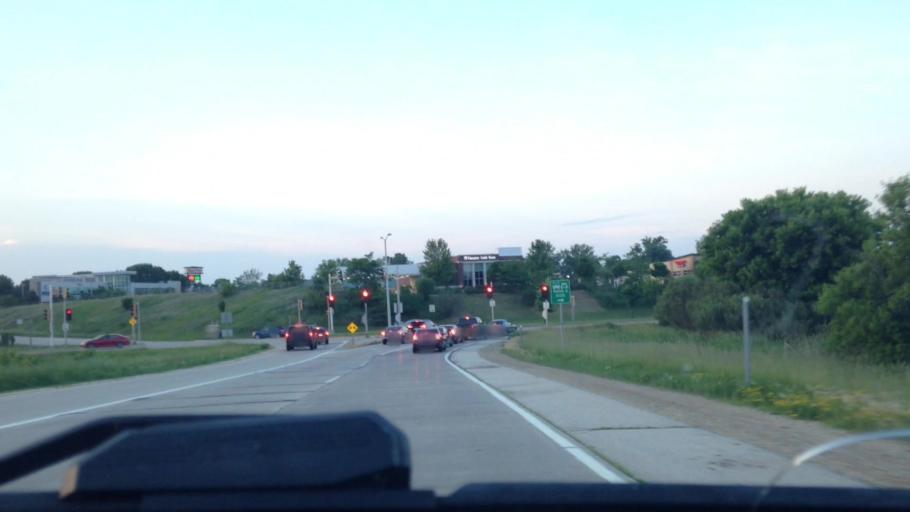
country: US
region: Wisconsin
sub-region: Washington County
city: West Bend
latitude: 43.3968
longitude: -88.1902
